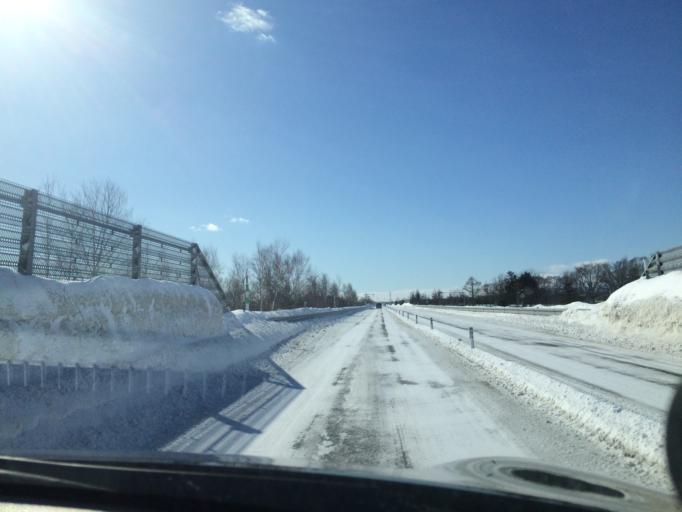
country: JP
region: Hokkaido
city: Chitose
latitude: 42.8760
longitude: 141.6166
